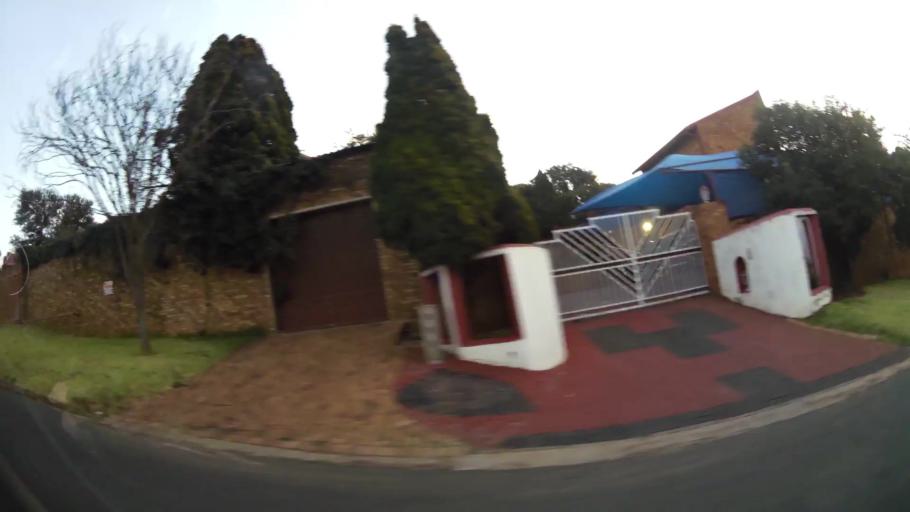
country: ZA
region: Gauteng
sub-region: West Rand District Municipality
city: Krugersdorp
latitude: -26.0751
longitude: 27.7777
